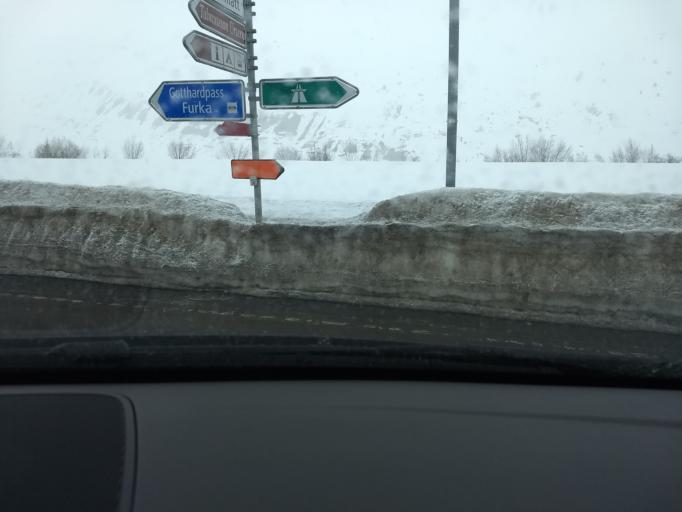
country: CH
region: Uri
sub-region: Uri
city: Andermatt
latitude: 46.6306
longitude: 8.5869
